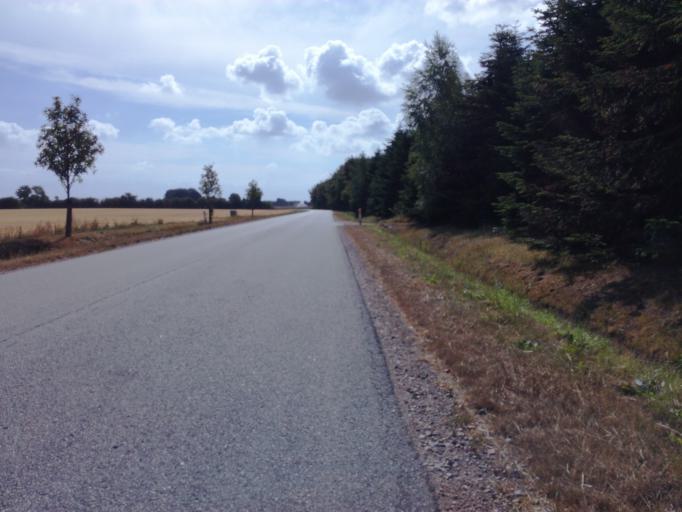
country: DK
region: South Denmark
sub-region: Vejle Kommune
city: Brejning
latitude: 55.6337
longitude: 9.6785
